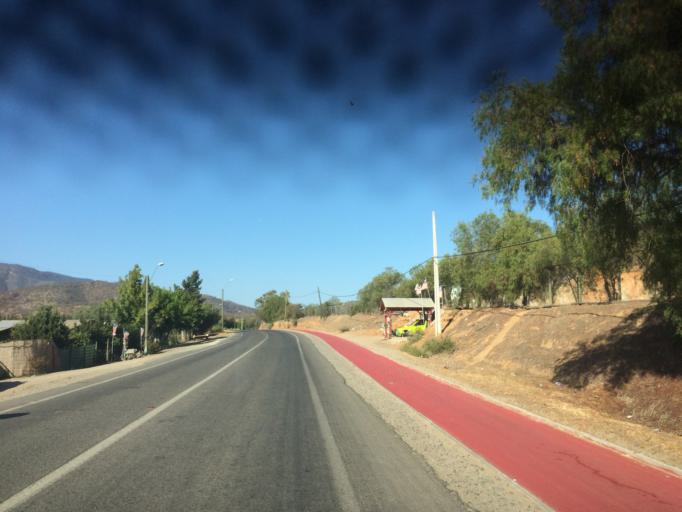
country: CL
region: Santiago Metropolitan
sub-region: Provincia de Melipilla
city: Melipilla
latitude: -33.4929
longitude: -71.1525
